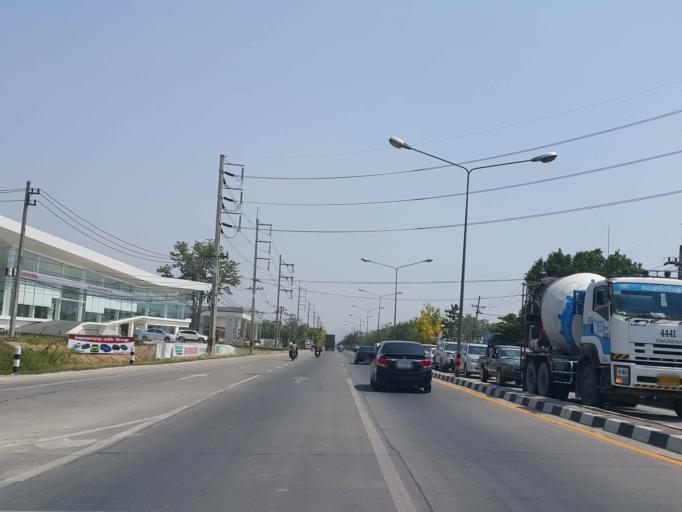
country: TH
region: Chiang Mai
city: San Sai
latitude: 18.8474
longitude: 99.0137
